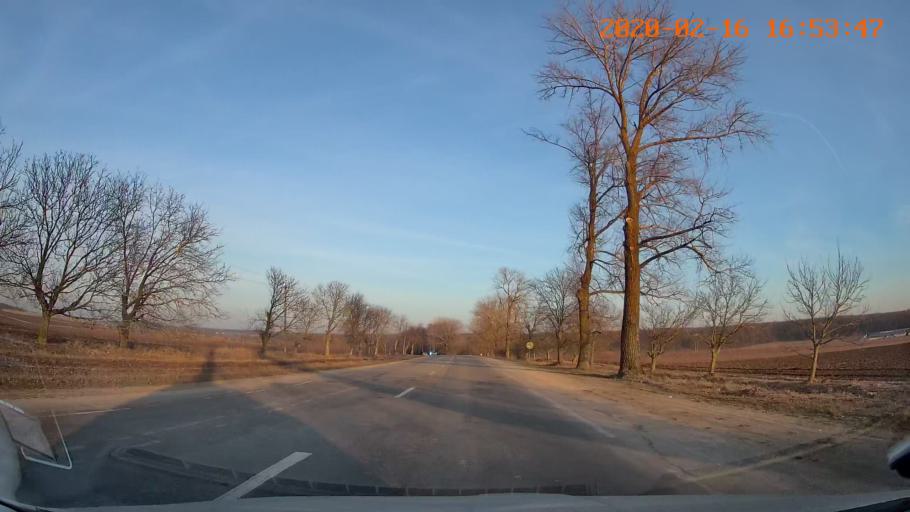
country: MD
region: Briceni
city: Briceni
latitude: 48.3162
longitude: 26.9930
